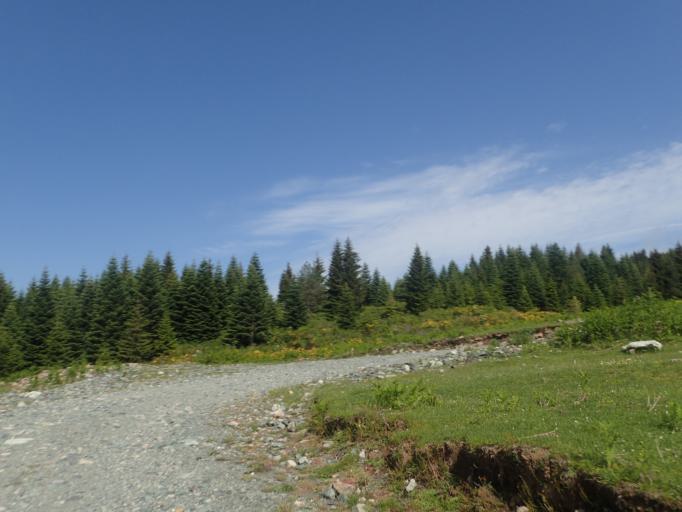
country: TR
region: Ordu
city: Kabaduz
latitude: 40.6895
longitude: 37.9432
